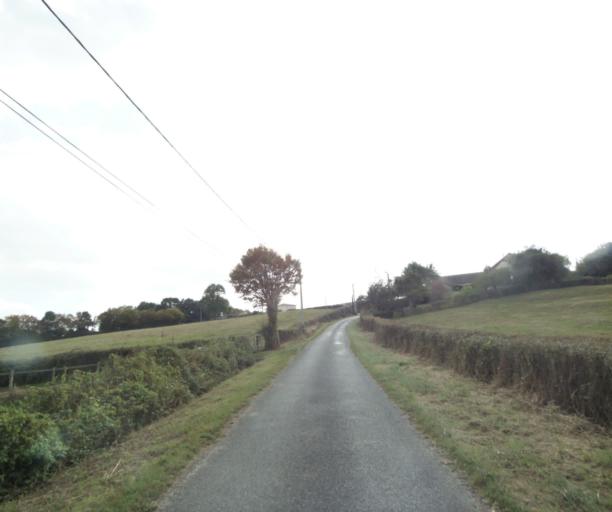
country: FR
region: Bourgogne
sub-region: Departement de Saone-et-Loire
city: Palinges
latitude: 46.4908
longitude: 4.2118
